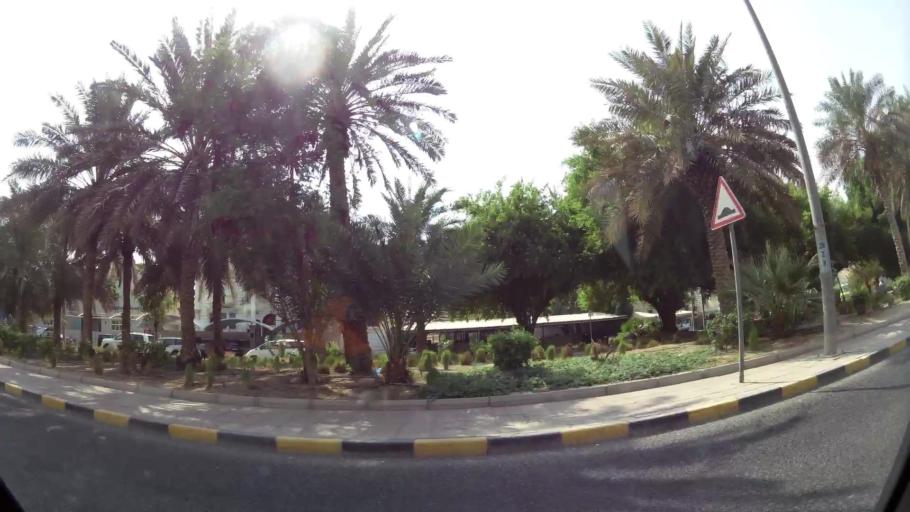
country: KW
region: Al Asimah
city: Ar Rabiyah
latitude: 29.3031
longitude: 47.8899
